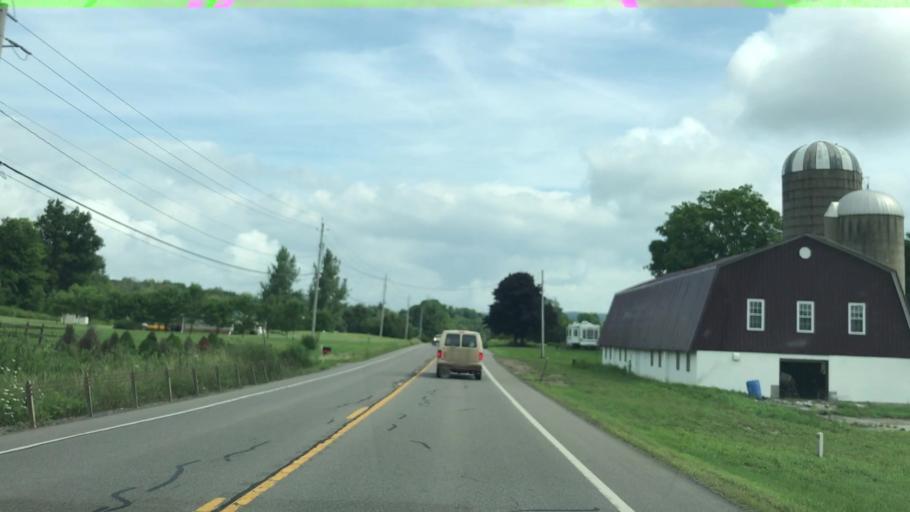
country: US
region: New York
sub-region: Steuben County
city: Bath
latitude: 42.4783
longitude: -77.2933
